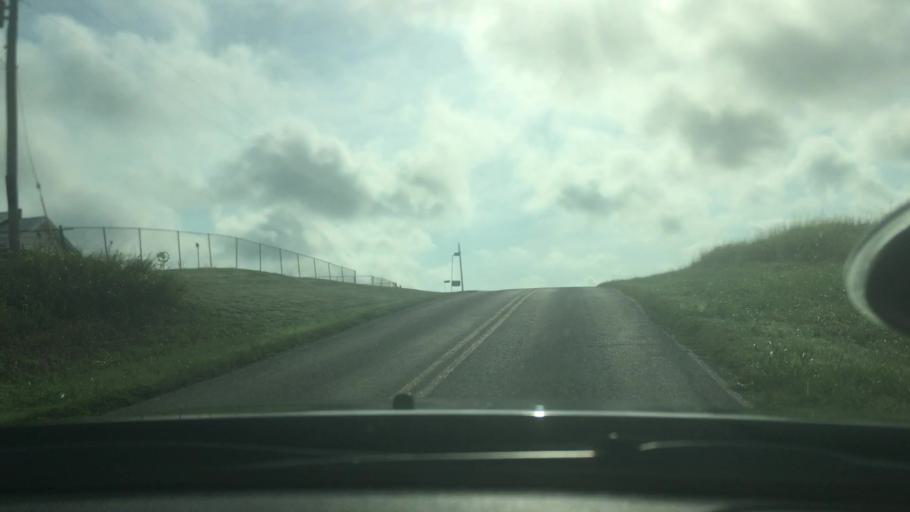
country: US
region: Oklahoma
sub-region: Pontotoc County
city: Ada
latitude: 34.6946
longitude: -96.5378
